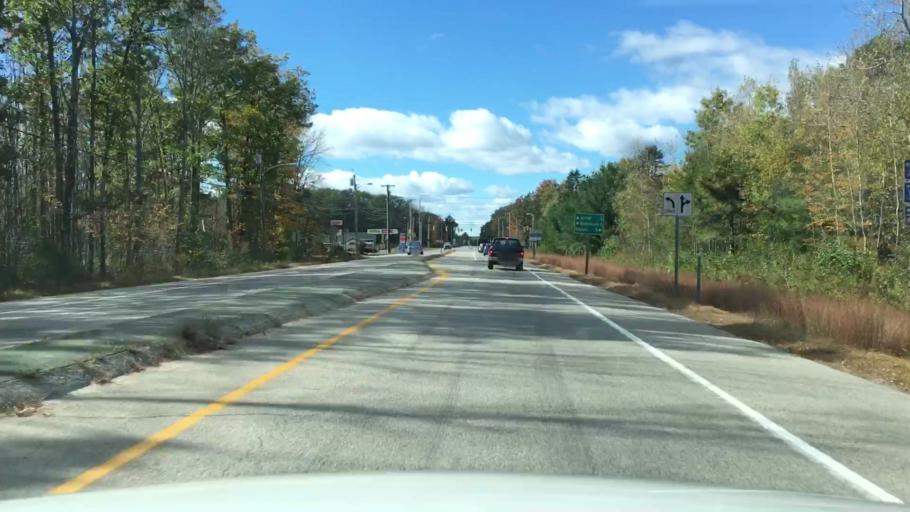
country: US
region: Maine
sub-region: York County
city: West Kennebunk
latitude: 43.4796
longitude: -70.6017
